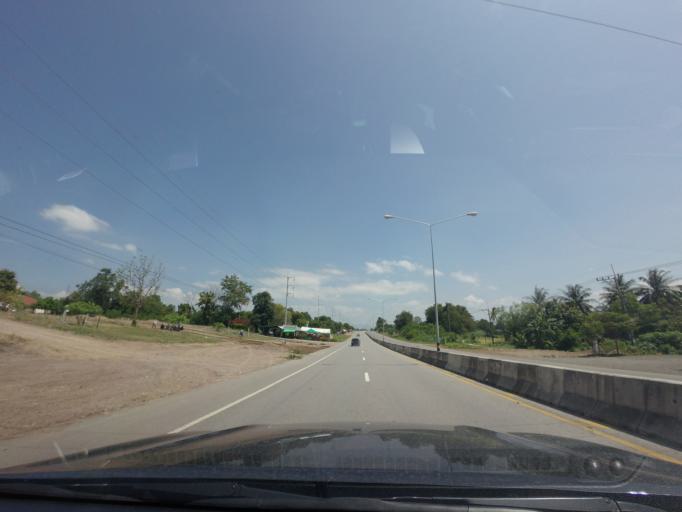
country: TH
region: Phetchabun
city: Lom Sak
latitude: 16.7644
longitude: 101.1517
